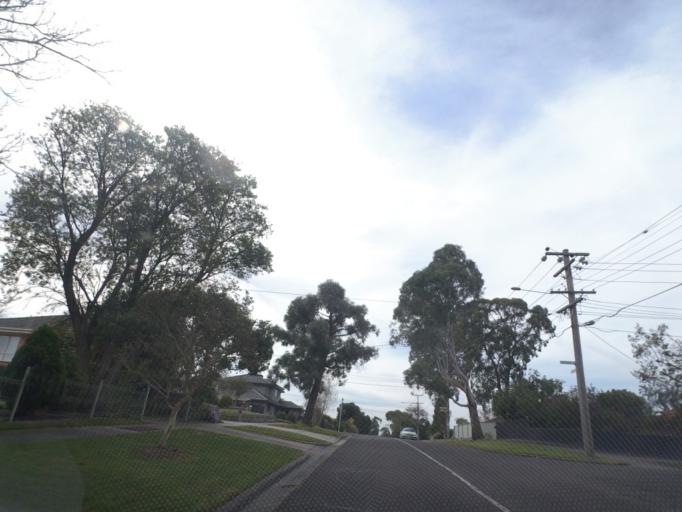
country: AU
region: Victoria
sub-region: Whitehorse
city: Vermont
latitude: -37.8307
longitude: 145.2029
